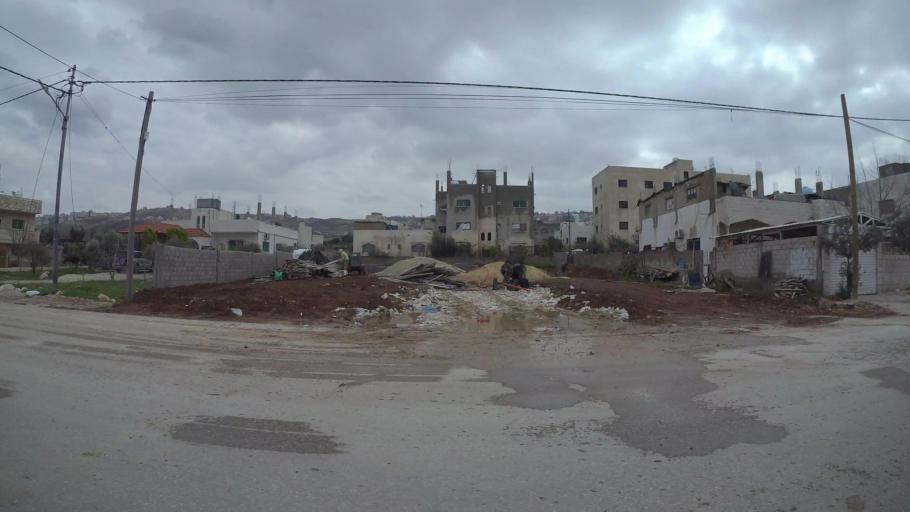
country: JO
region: Amman
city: Al Jubayhah
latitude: 32.0548
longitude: 35.8424
